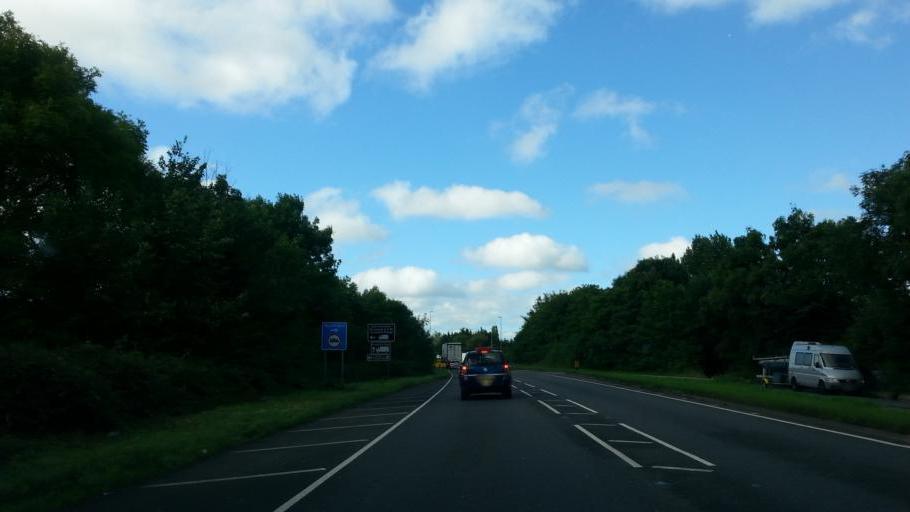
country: GB
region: England
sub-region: Northamptonshire
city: Broughton
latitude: 52.3111
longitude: -0.8146
